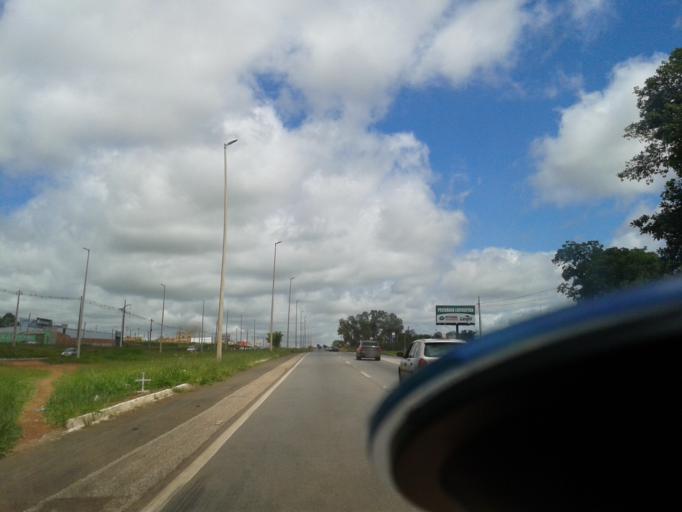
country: BR
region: Goias
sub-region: Goianira
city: Goianira
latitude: -16.5867
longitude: -49.3828
